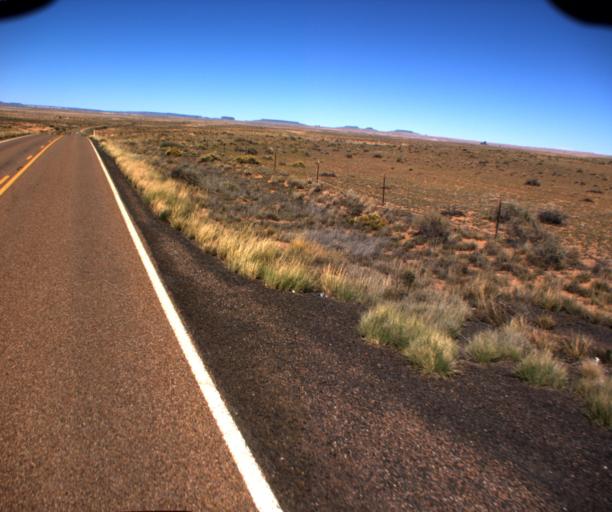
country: US
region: Arizona
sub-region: Navajo County
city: Holbrook
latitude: 35.0459
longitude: -110.0936
